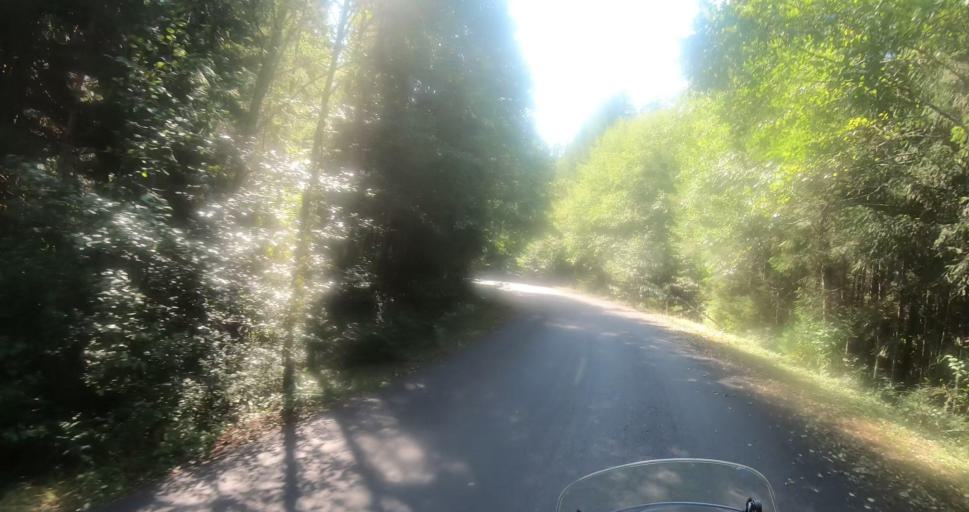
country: US
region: Washington
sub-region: Skamania County
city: Carson
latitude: 46.1818
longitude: -121.8528
